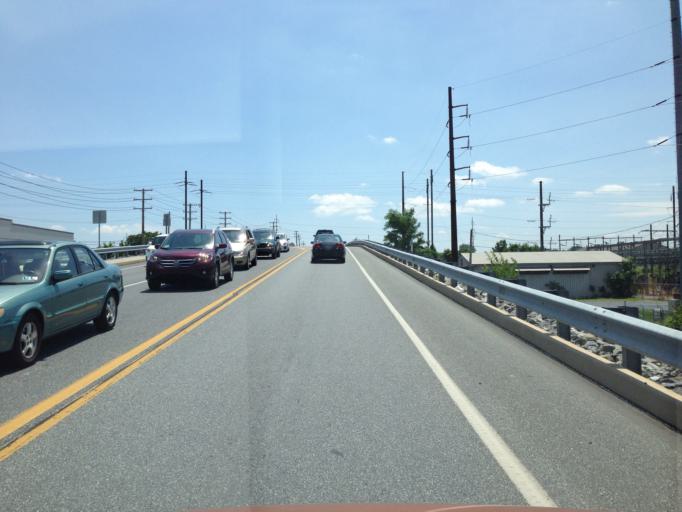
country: US
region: Pennsylvania
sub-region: Lancaster County
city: Lancaster
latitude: 40.0590
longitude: -76.3206
